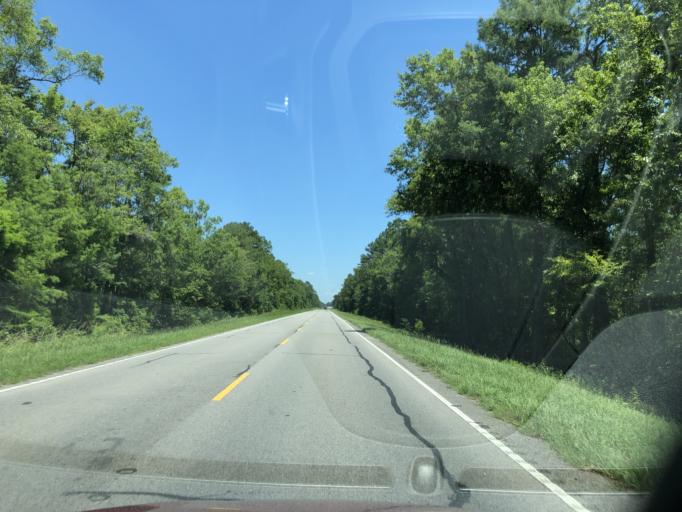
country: US
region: South Carolina
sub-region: Orangeburg County
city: Branchville
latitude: 33.2354
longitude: -80.8745
